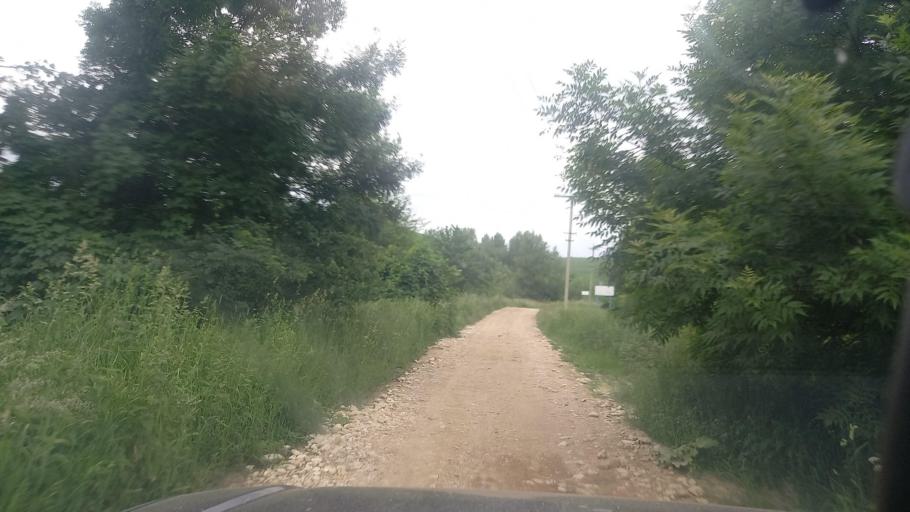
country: RU
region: Krasnodarskiy
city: Peredovaya
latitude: 44.0851
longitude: 41.3720
